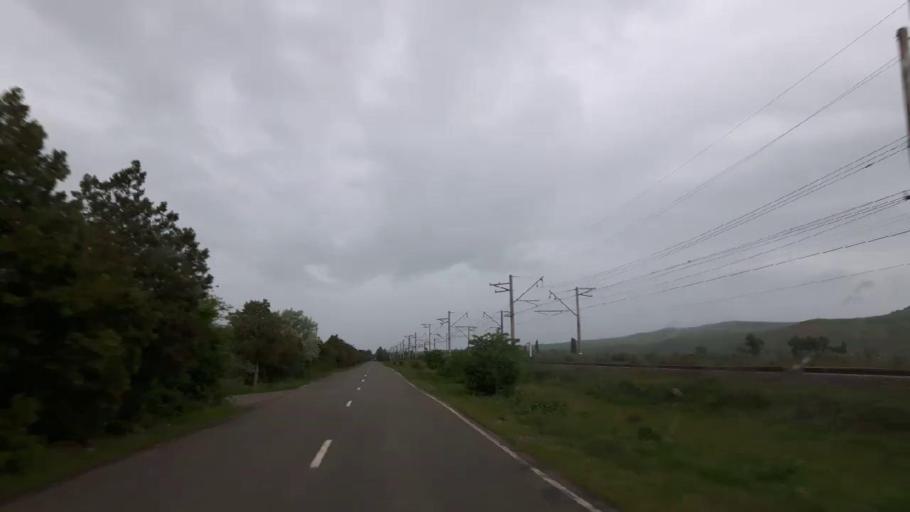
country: GE
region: Shida Kartli
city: Gori
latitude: 41.9965
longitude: 44.0184
